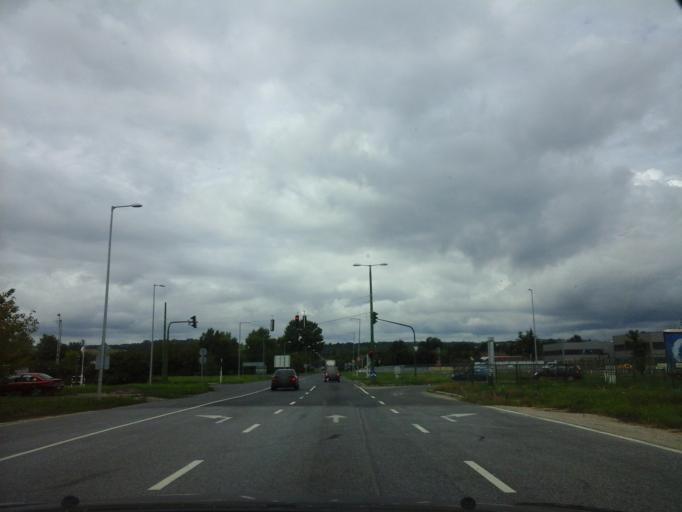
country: HU
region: Borsod-Abauj-Zemplen
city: Szirmabesenyo
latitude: 48.1303
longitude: 20.8001
